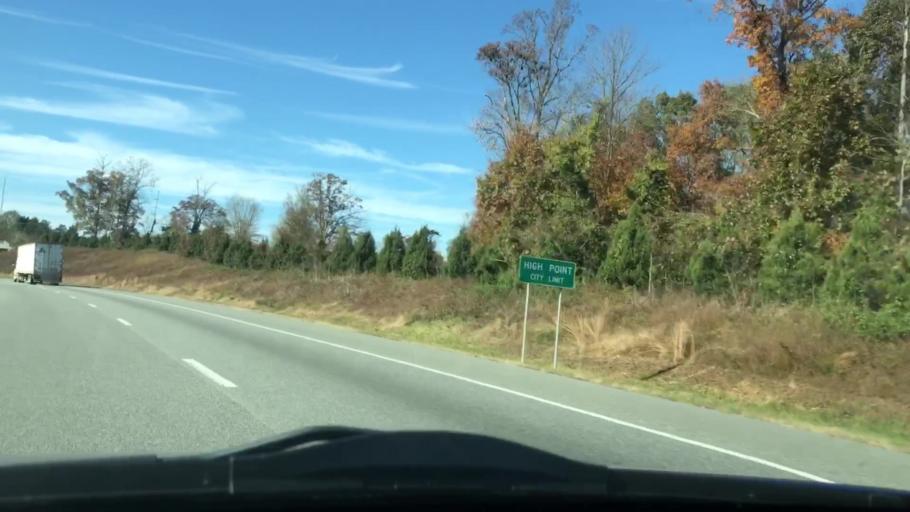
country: US
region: North Carolina
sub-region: Randolph County
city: Archdale
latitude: 35.9387
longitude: -79.9607
